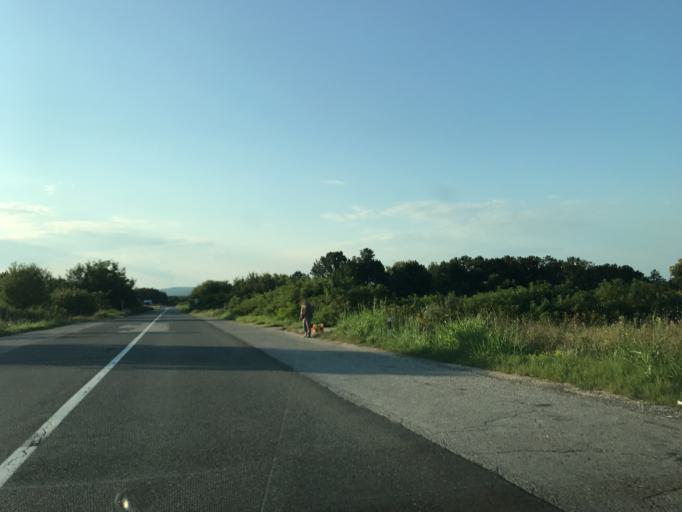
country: RO
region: Mehedinti
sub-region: Comuna Gogosu
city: Ostrovu Mare
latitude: 44.4379
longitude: 22.4584
